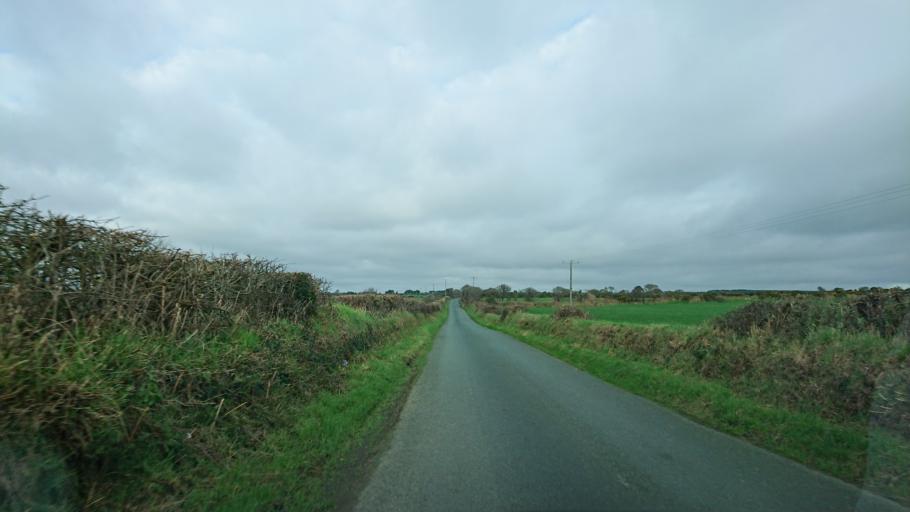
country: IE
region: Munster
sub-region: Waterford
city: Portlaw
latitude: 52.1542
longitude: -7.3094
